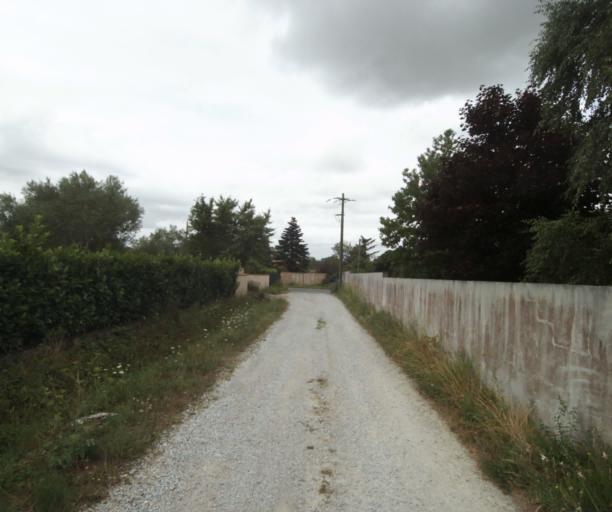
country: FR
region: Midi-Pyrenees
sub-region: Departement du Tarn
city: Soreze
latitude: 43.4478
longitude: 2.0600
